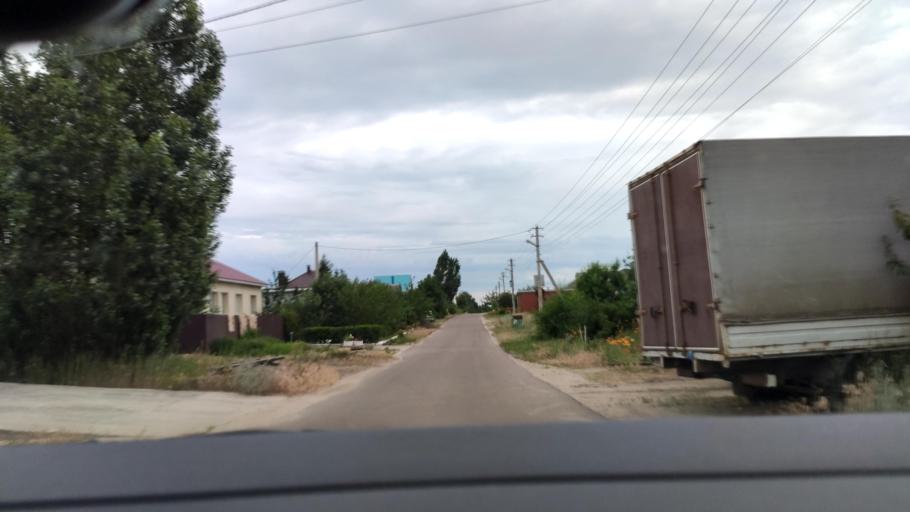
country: RU
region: Voronezj
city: Maslovka
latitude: 51.5691
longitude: 39.2503
